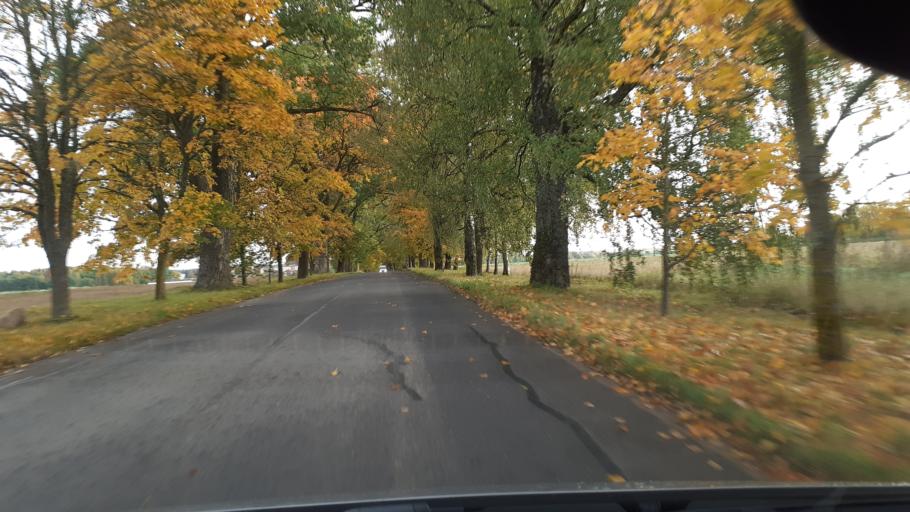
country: LV
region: Kuldigas Rajons
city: Kuldiga
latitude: 57.0087
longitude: 21.8960
